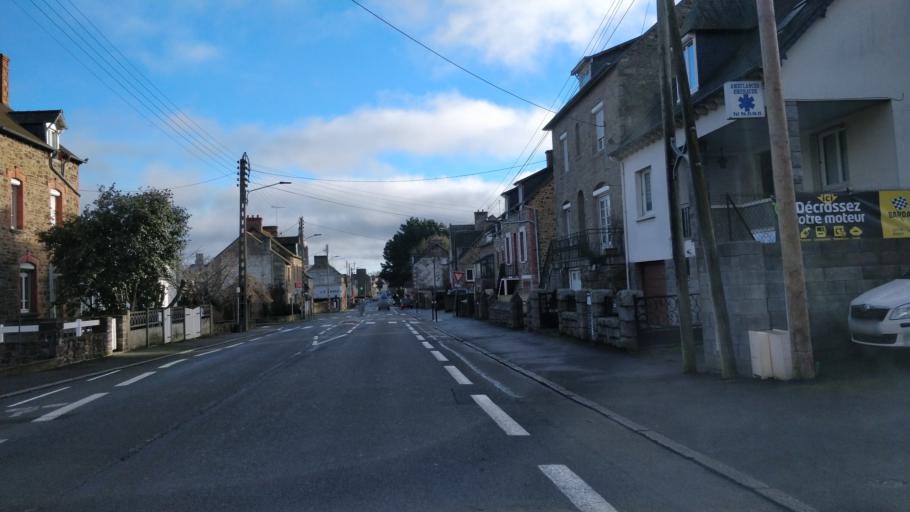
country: FR
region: Brittany
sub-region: Departement des Cotes-d'Armor
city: Lamballe
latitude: 48.4663
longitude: -2.5239
